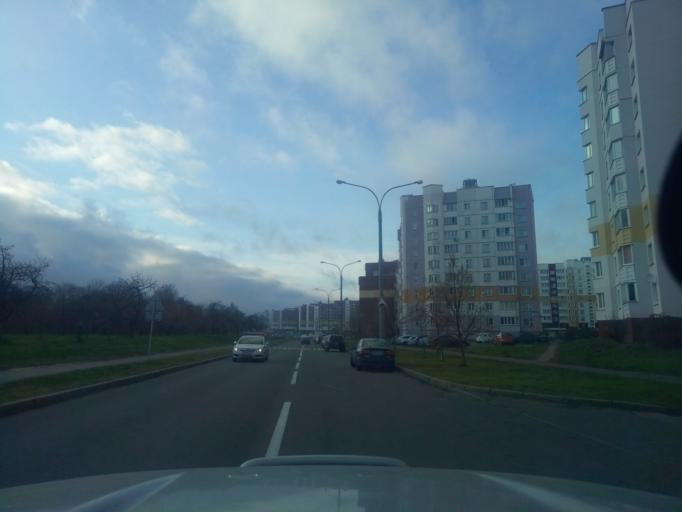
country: BY
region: Minsk
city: Novoye Medvezhino
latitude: 53.8768
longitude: 27.4852
